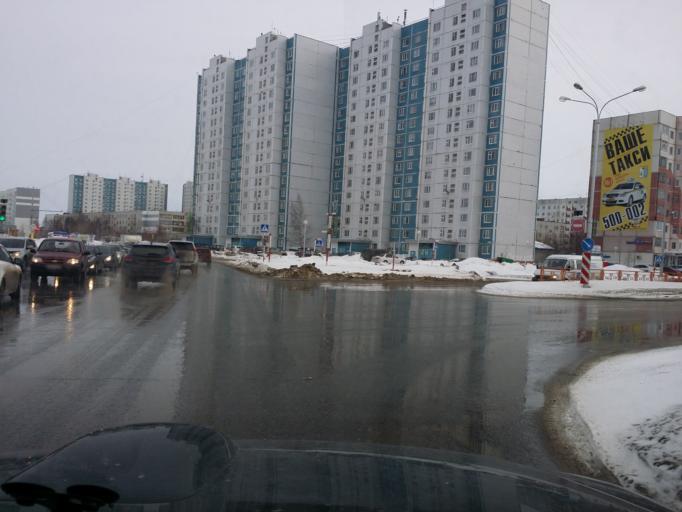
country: RU
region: Khanty-Mansiyskiy Avtonomnyy Okrug
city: Nizhnevartovsk
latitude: 60.9515
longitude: 76.6081
